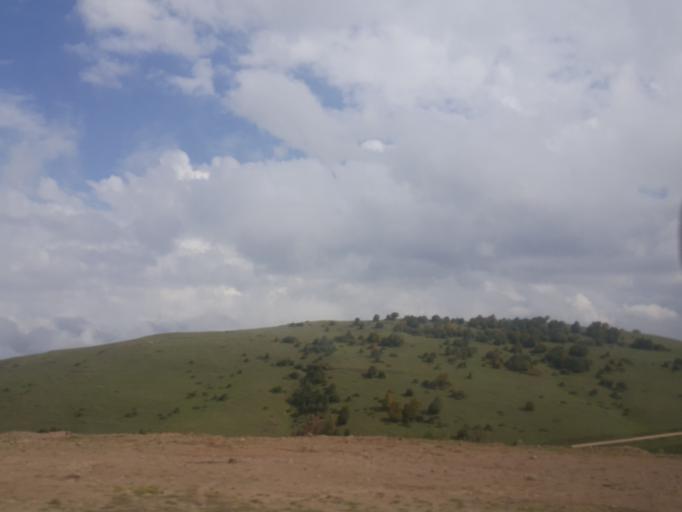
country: TR
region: Tokat
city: Bereketli
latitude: 40.5763
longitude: 37.3034
